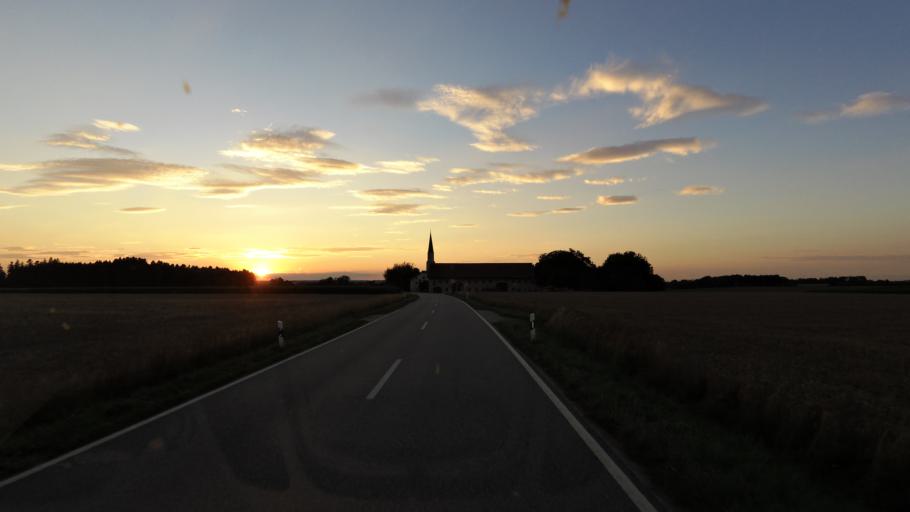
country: DE
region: Bavaria
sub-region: Upper Bavaria
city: Taufkirchen
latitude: 48.1652
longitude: 12.4399
